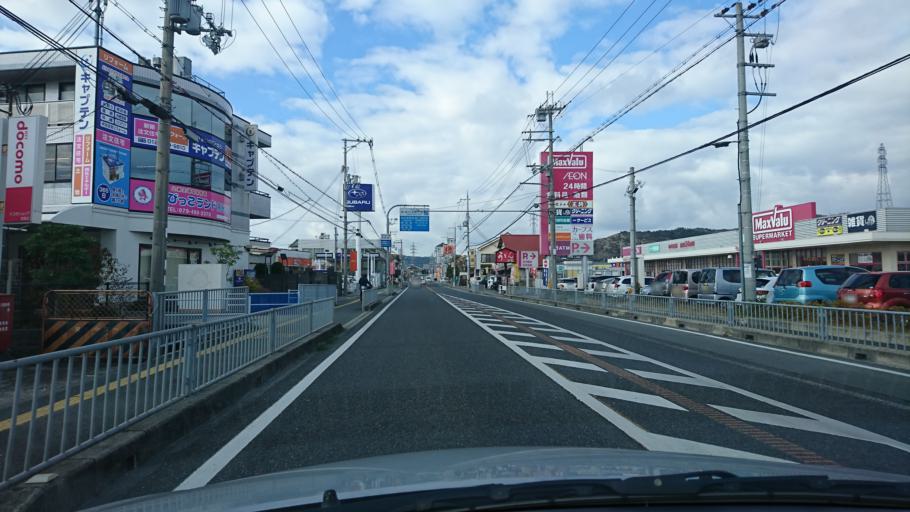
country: JP
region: Hyogo
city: Kakogawacho-honmachi
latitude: 34.7857
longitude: 134.8067
